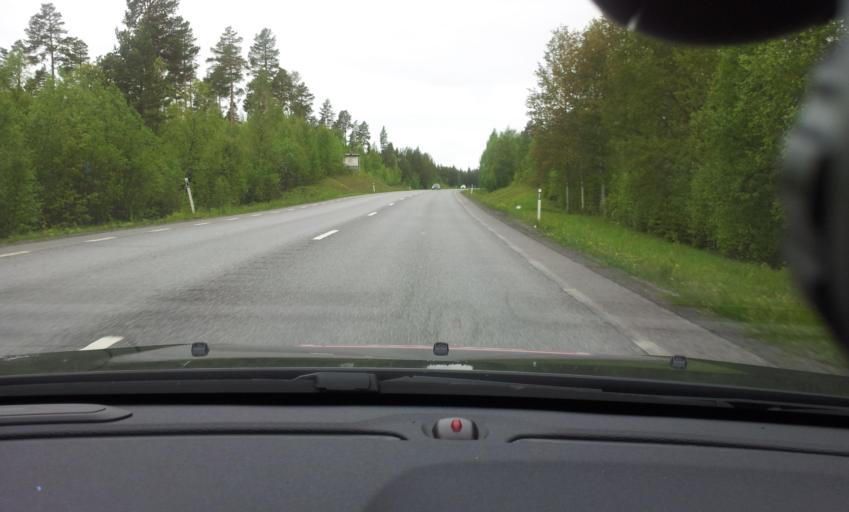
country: SE
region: Jaemtland
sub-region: Krokoms Kommun
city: Krokom
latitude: 63.3132
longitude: 14.1366
